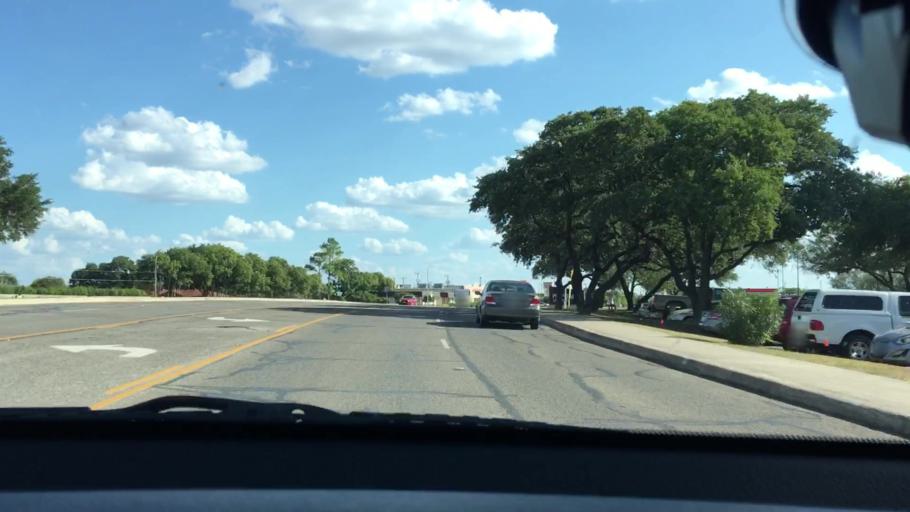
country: US
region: Texas
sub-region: Bexar County
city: Universal City
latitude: 29.5569
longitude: -98.3085
